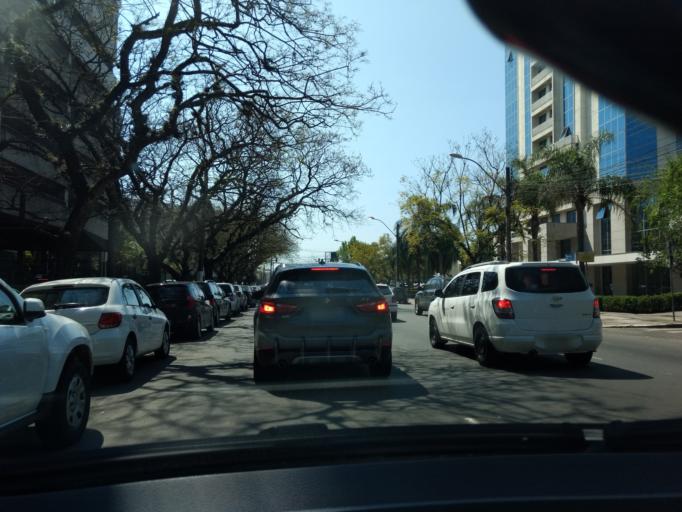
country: BR
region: Rio Grande do Sul
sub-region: Porto Alegre
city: Porto Alegre
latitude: -30.0238
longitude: -51.1613
